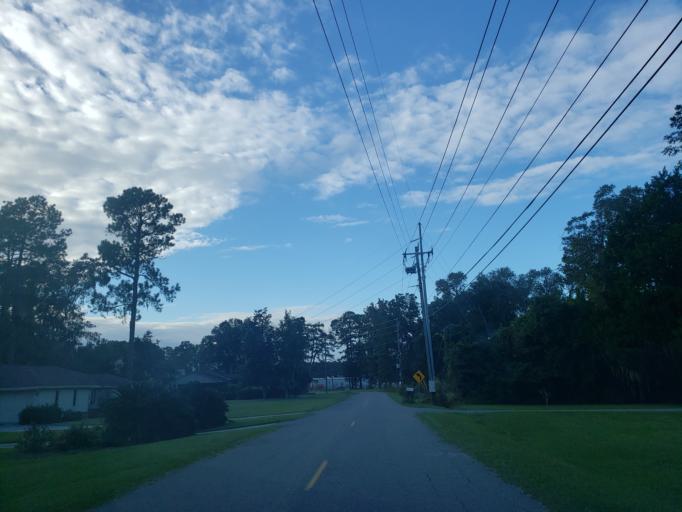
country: US
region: Georgia
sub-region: Chatham County
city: Georgetown
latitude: 31.9884
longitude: -81.2257
